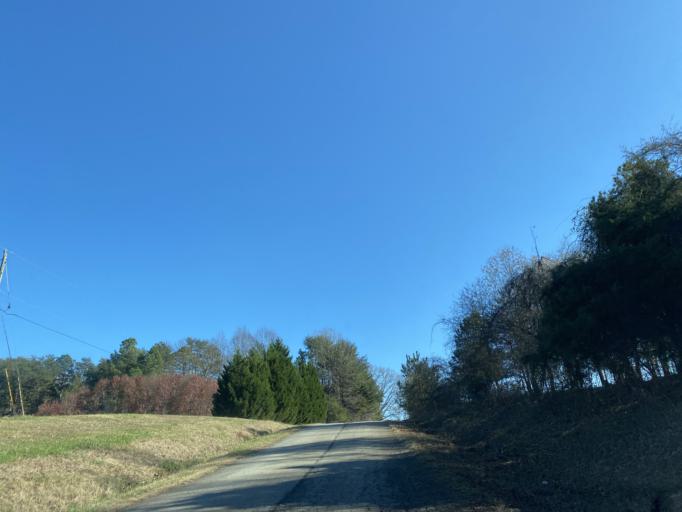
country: US
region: South Carolina
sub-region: Spartanburg County
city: Mayo
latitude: 35.1462
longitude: -81.7806
